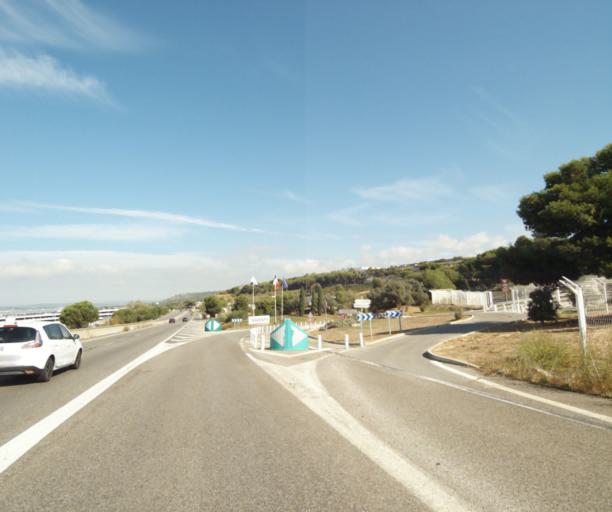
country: FR
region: Provence-Alpes-Cote d'Azur
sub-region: Departement des Bouches-du-Rhone
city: Saint-Victoret
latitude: 43.4326
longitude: 5.2350
